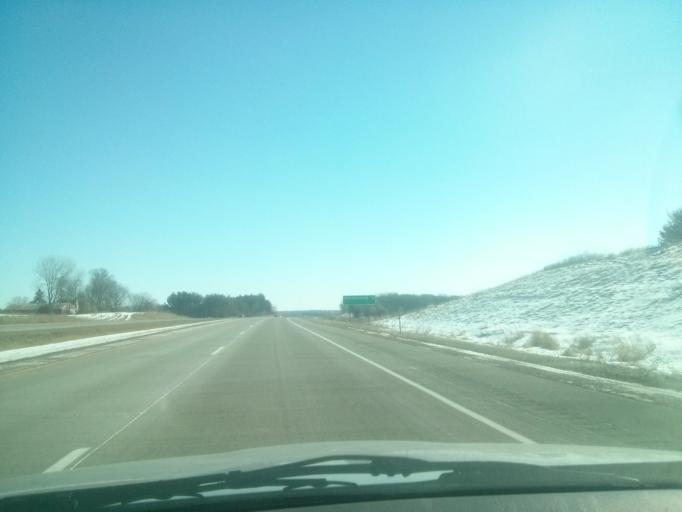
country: US
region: Wisconsin
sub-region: Saint Croix County
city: Somerset
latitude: 45.1077
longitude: -92.7109
